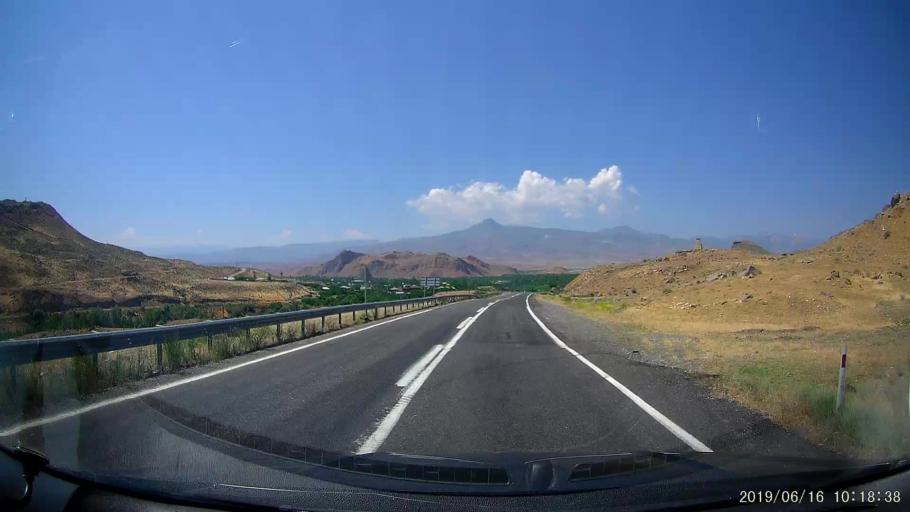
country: TR
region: Igdir
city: Tuzluca
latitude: 40.1584
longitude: 43.6657
